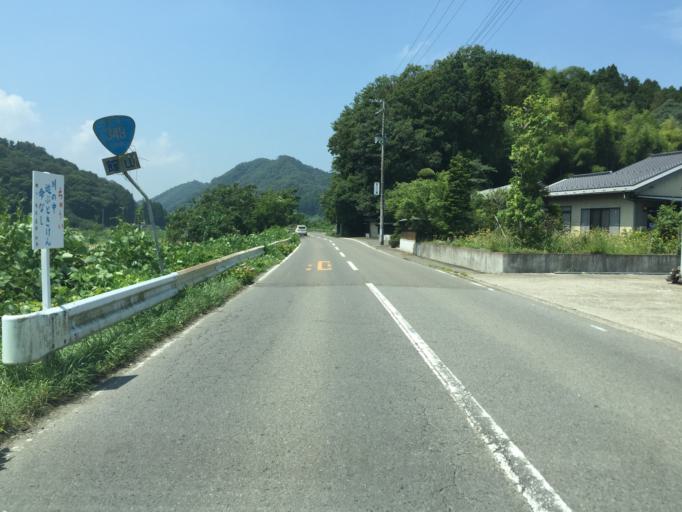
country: JP
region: Miyagi
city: Marumori
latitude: 37.9226
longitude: 140.7627
